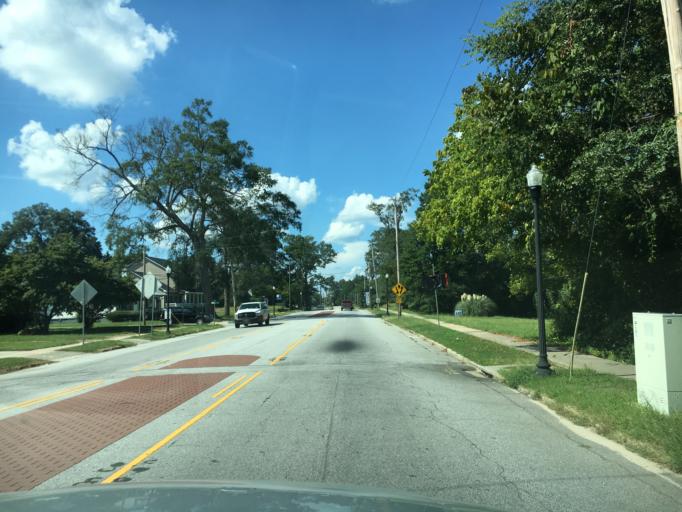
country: US
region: South Carolina
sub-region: Laurens County
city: Clinton
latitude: 34.4777
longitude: -81.8810
